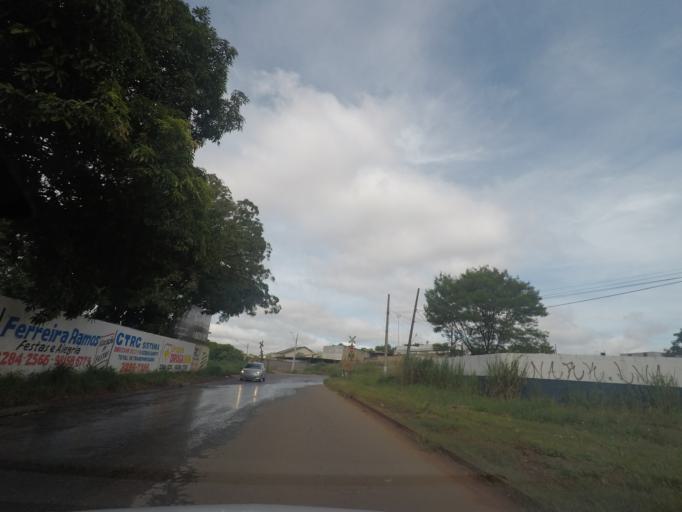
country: BR
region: Goias
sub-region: Goiania
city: Goiania
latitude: -16.6744
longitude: -49.2005
